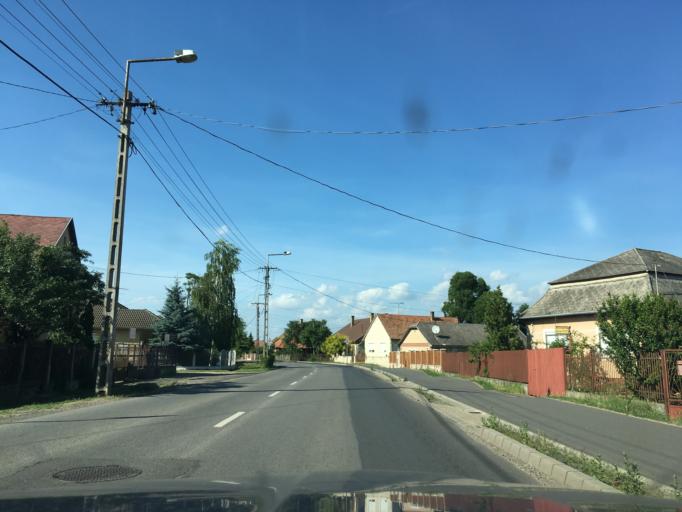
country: HU
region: Hajdu-Bihar
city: Hajdusamson
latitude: 47.6041
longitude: 21.7630
